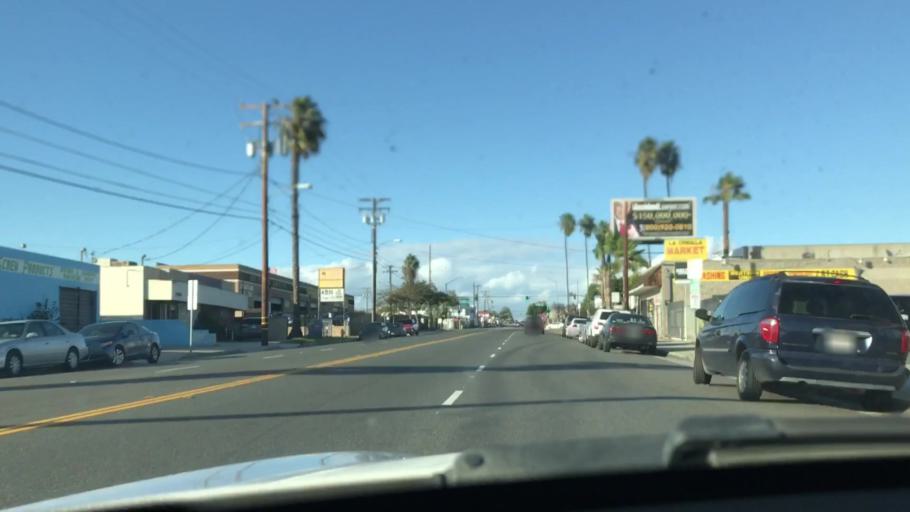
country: US
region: California
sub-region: Los Angeles County
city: West Athens
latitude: 33.9110
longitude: -118.3004
